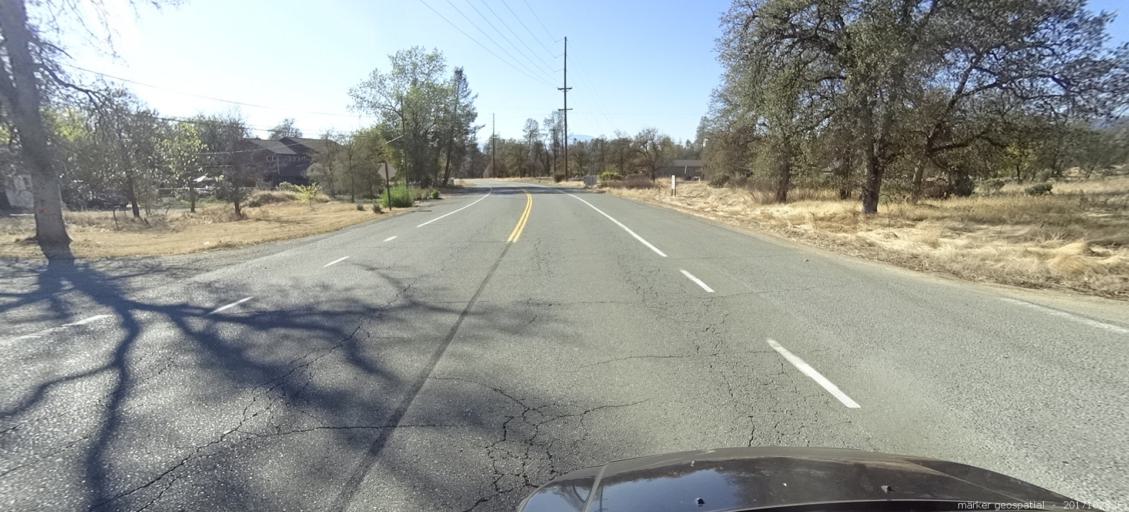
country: US
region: California
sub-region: Shasta County
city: Central Valley (historical)
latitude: 40.6421
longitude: -122.3714
